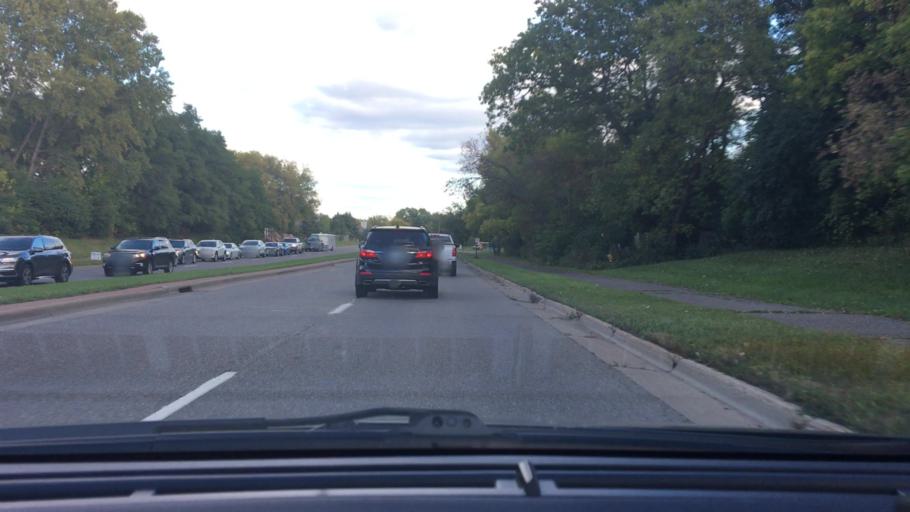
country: US
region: Minnesota
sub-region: Hennepin County
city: Maple Grove
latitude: 45.0621
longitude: -93.4365
